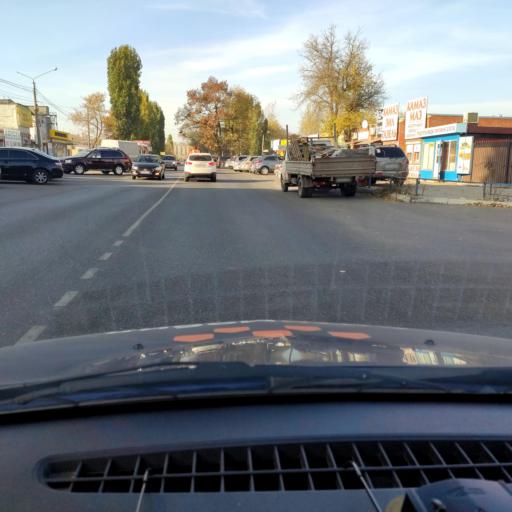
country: RU
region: Voronezj
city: Voronezh
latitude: 51.6640
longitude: 39.1384
